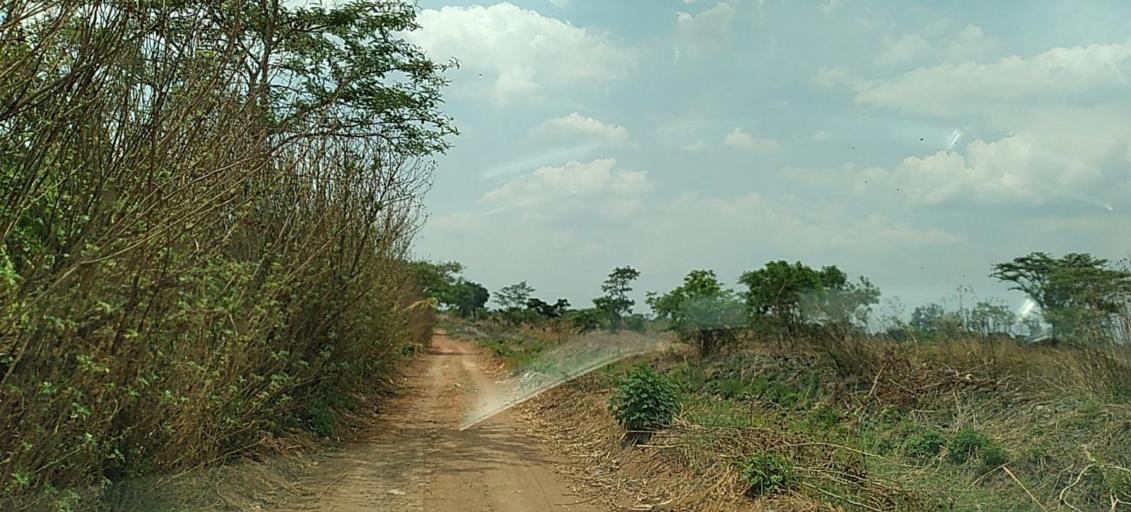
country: ZM
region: Copperbelt
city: Chililabombwe
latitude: -12.3686
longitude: 27.7997
